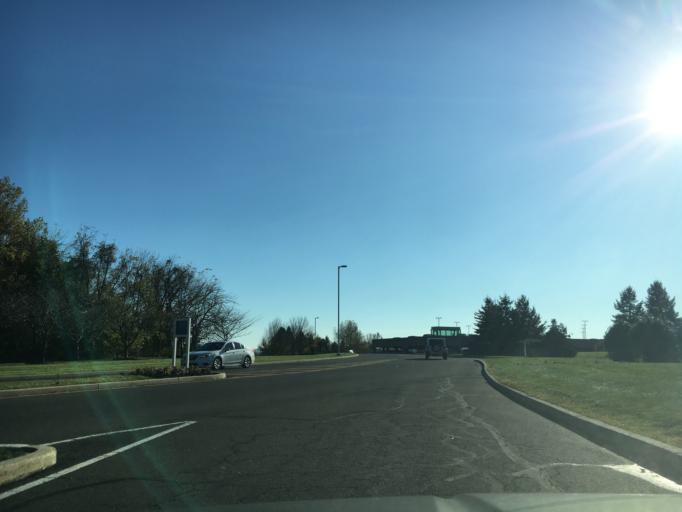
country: US
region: Pennsylvania
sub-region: Lehigh County
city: Fullerton
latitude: 40.6333
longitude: -75.4522
